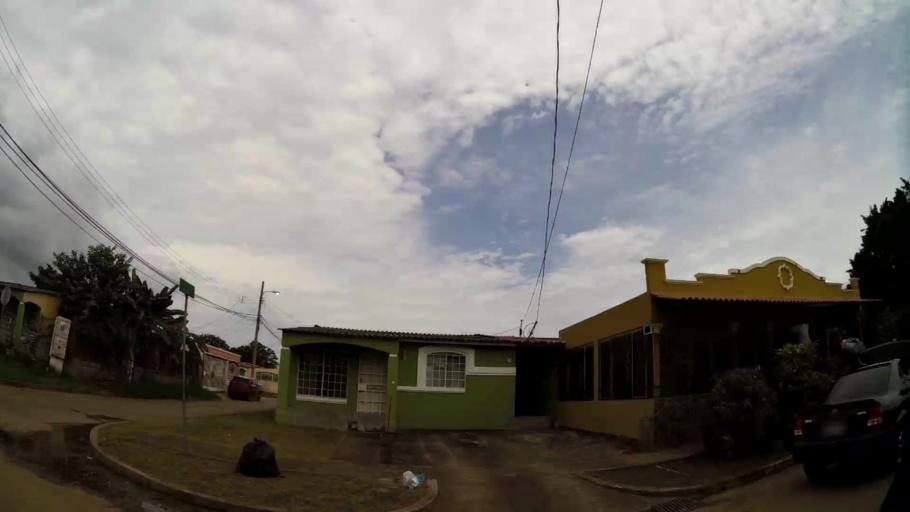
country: PA
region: Panama
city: Tocumen
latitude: 9.0405
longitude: -79.4071
